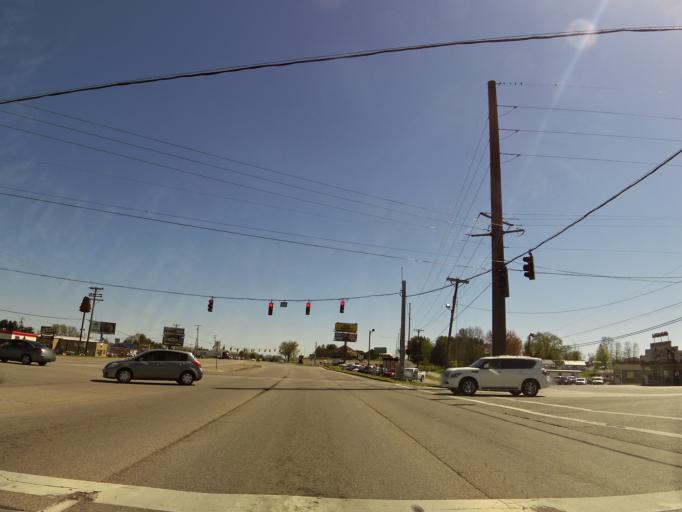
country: US
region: Kentucky
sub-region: Pulaski County
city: Somerset
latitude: 37.0316
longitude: -84.6274
